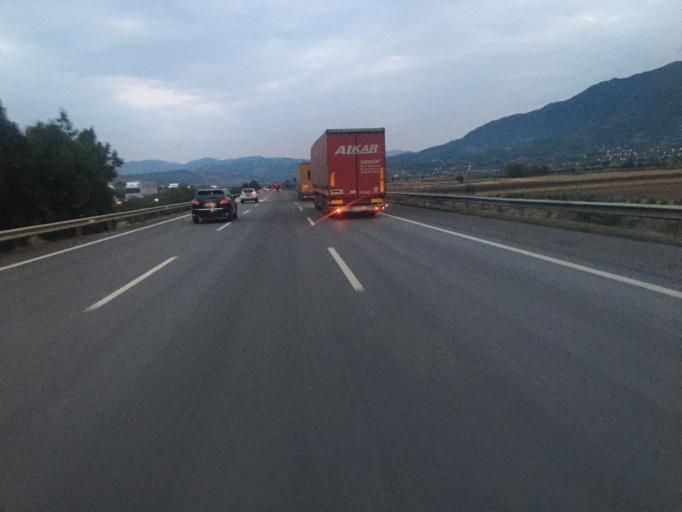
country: TR
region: Osmaniye
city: Osmaniye
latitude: 37.1442
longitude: 36.3293
